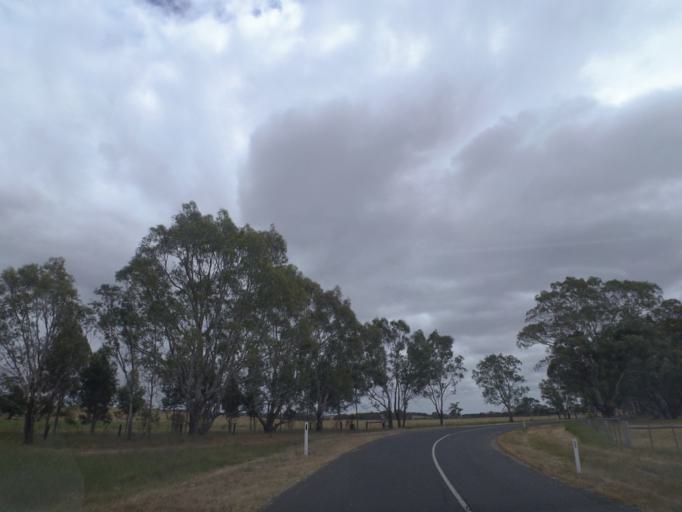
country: AU
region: Victoria
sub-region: Whittlesea
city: Whittlesea
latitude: -37.1080
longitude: 145.0211
